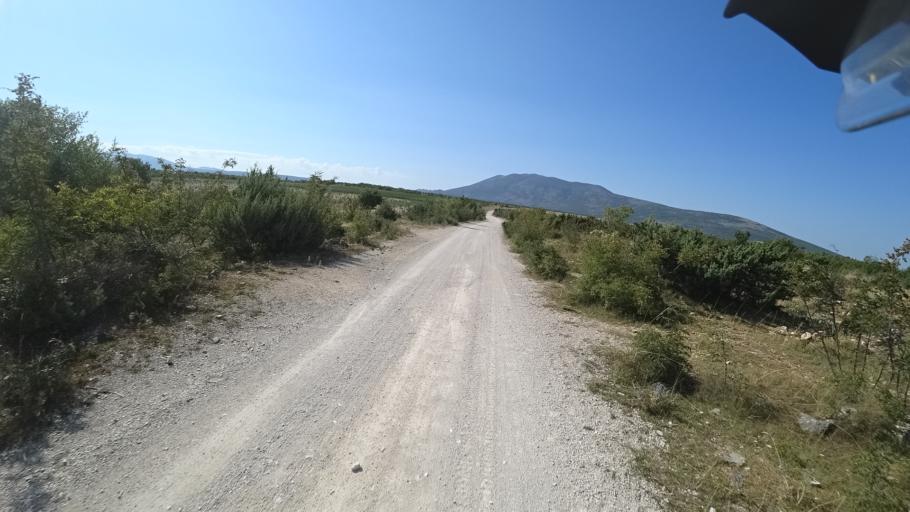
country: HR
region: Sibensko-Kniniska
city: Knin
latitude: 43.9945
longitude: 16.1933
